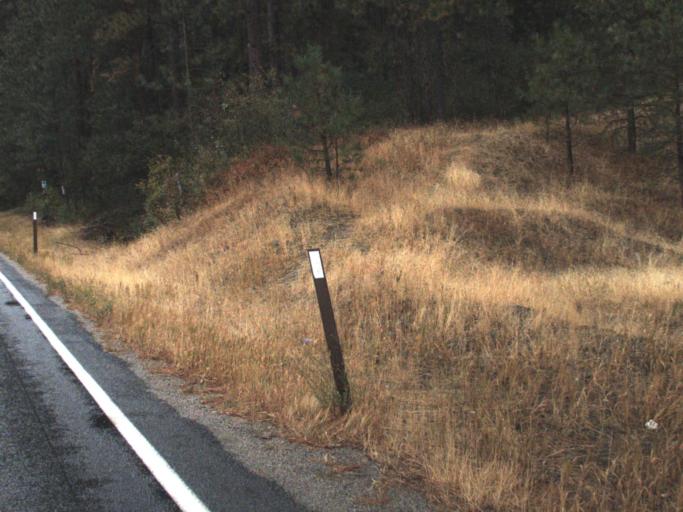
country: US
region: Washington
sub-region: Stevens County
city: Chewelah
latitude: 48.2025
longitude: -117.7313
